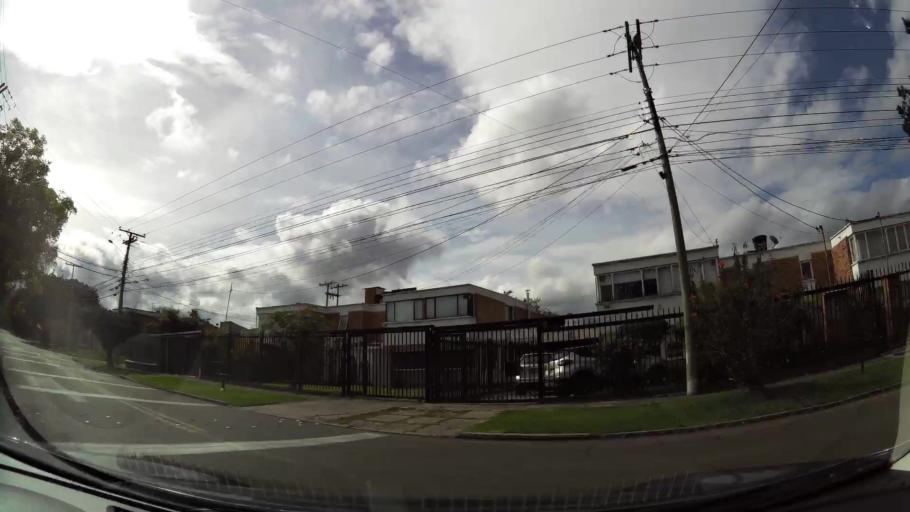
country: CO
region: Bogota D.C.
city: Barrio San Luis
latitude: 4.7061
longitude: -74.0755
